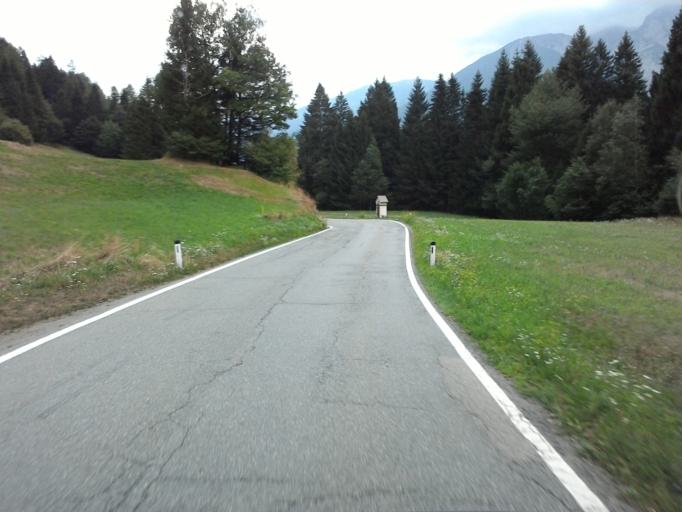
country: AT
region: Carinthia
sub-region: Politischer Bezirk Spittal an der Drau
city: Oberdrauburg
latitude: 46.6747
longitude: 12.9656
